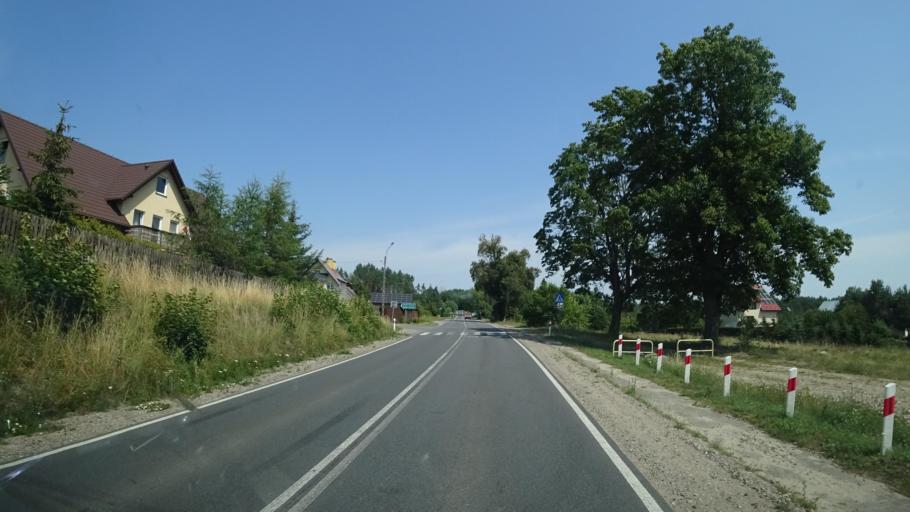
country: PL
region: Pomeranian Voivodeship
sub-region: Powiat koscierski
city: Dziemiany
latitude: 53.9742
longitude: 17.7676
